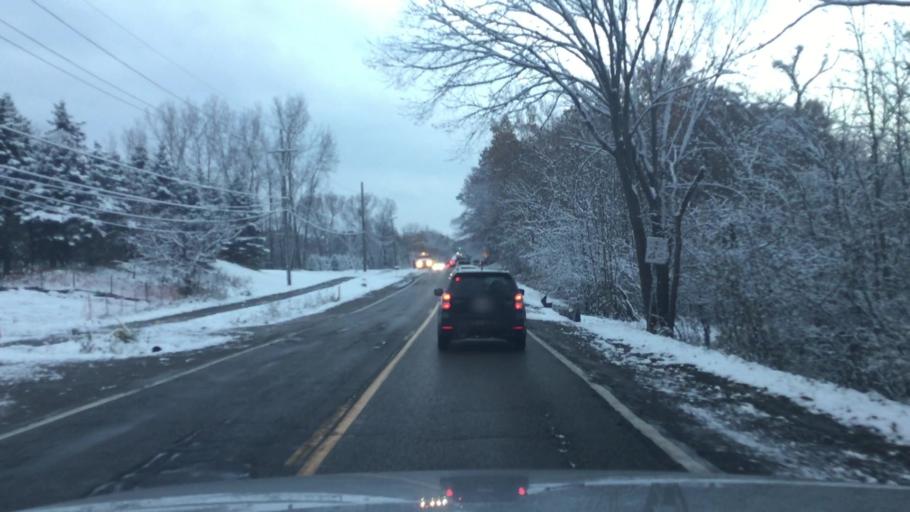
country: US
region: Michigan
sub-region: Oakland County
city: West Bloomfield Township
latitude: 42.6003
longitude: -83.3979
